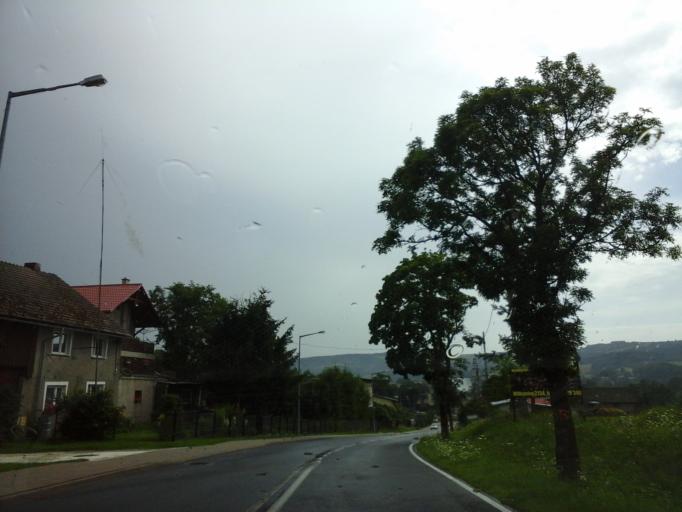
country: PL
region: Lower Silesian Voivodeship
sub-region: Powiat klodzki
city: Miedzylesie
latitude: 50.1536
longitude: 16.6703
